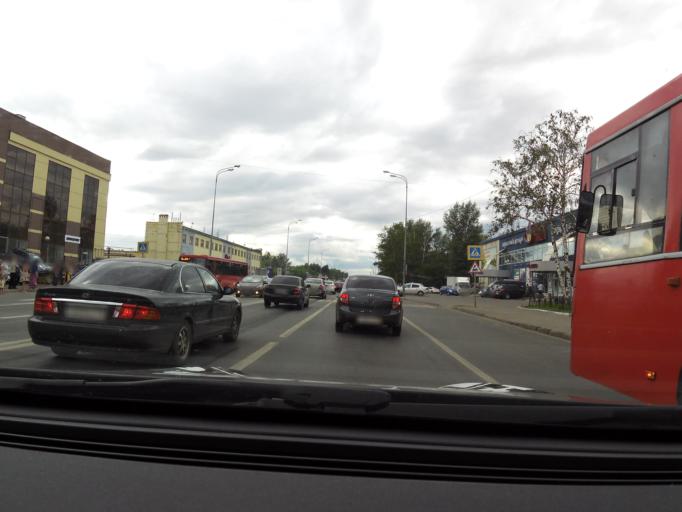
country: RU
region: Tatarstan
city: Staroye Arakchino
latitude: 55.8269
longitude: 49.0260
